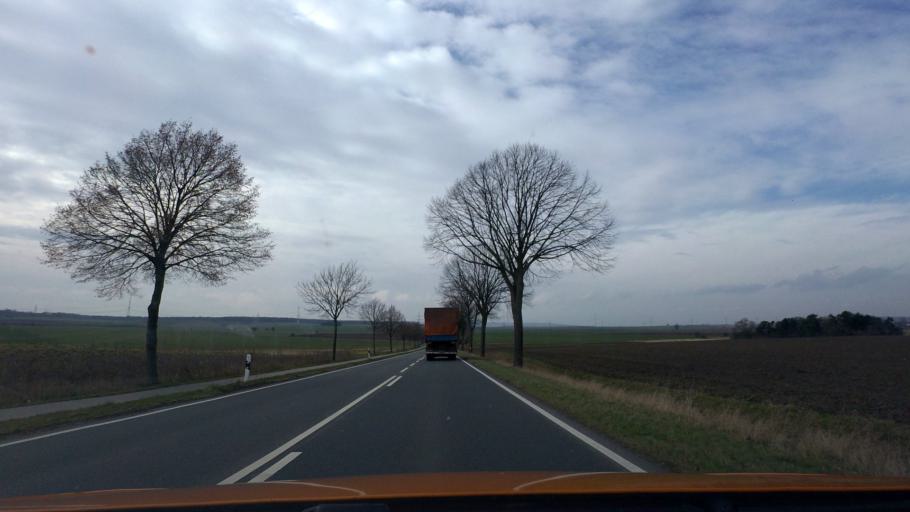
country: DE
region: Lower Saxony
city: Helmstedt
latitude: 52.2282
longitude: 10.9834
